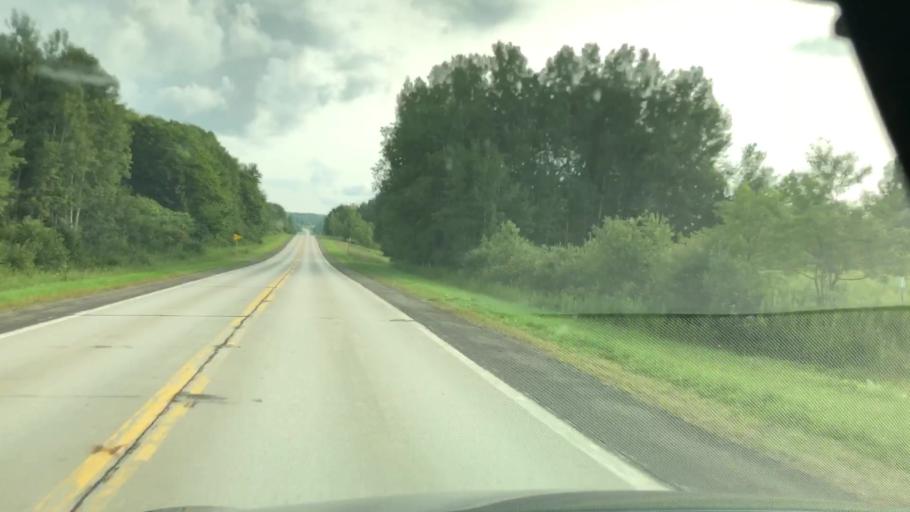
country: US
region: Pennsylvania
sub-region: Erie County
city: Union City
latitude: 41.9774
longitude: -79.8416
